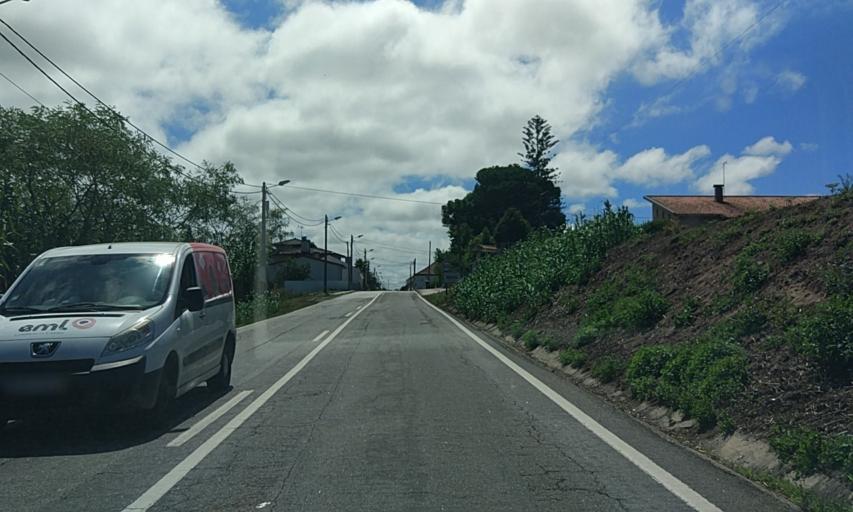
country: PT
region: Aveiro
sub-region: Vagos
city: Vagos
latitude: 40.5656
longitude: -8.6826
